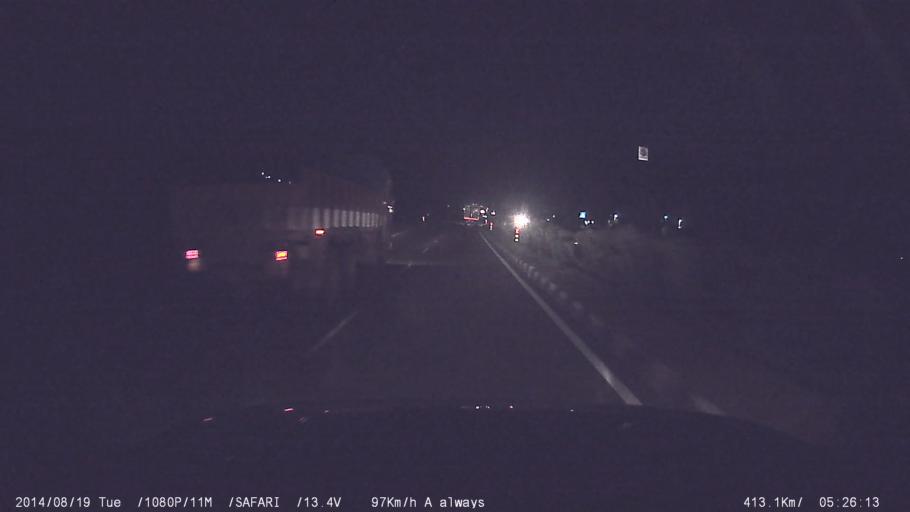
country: IN
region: Tamil Nadu
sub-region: Salem
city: Attayyampatti
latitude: 11.5805
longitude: 78.0512
